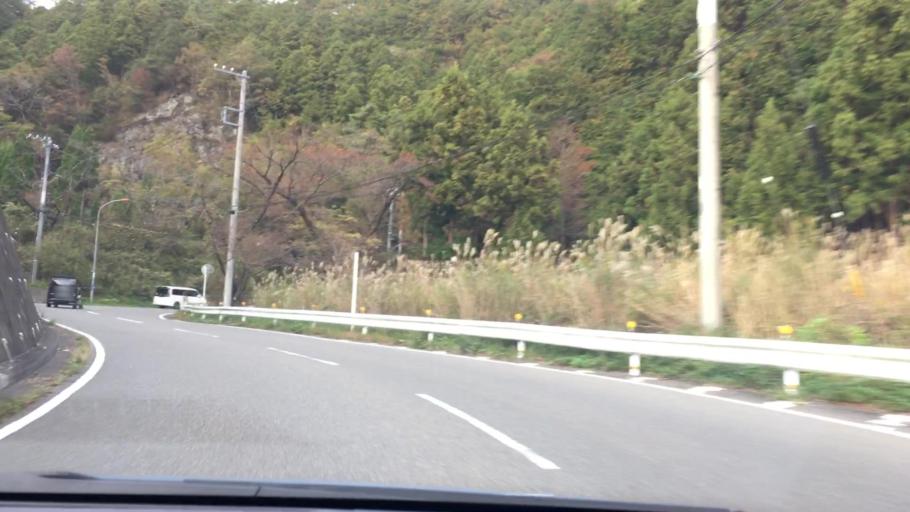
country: JP
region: Yamanashi
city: Uenohara
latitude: 35.5585
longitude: 139.1404
